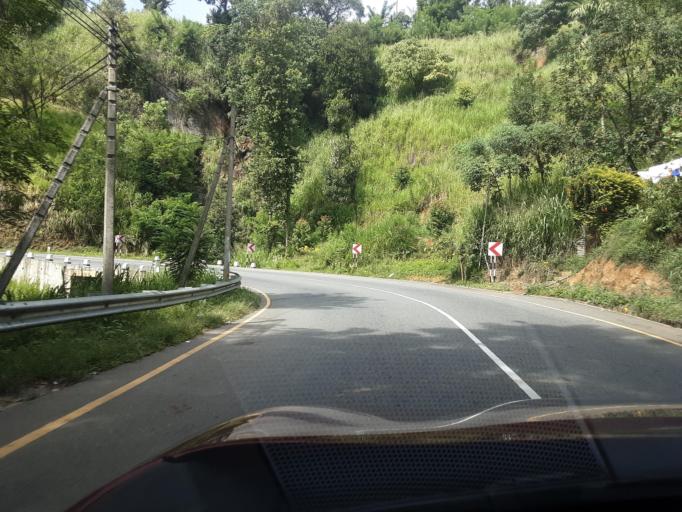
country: LK
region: Uva
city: Badulla
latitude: 6.9659
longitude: 81.0902
